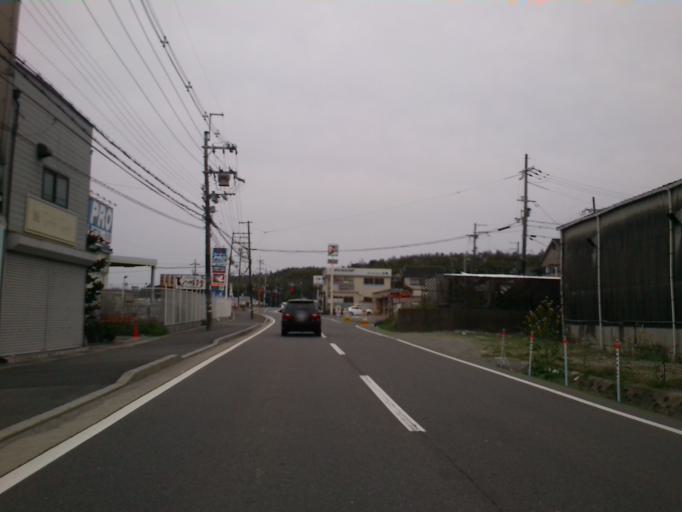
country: JP
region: Kyoto
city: Yawata
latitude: 34.8563
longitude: 135.7136
